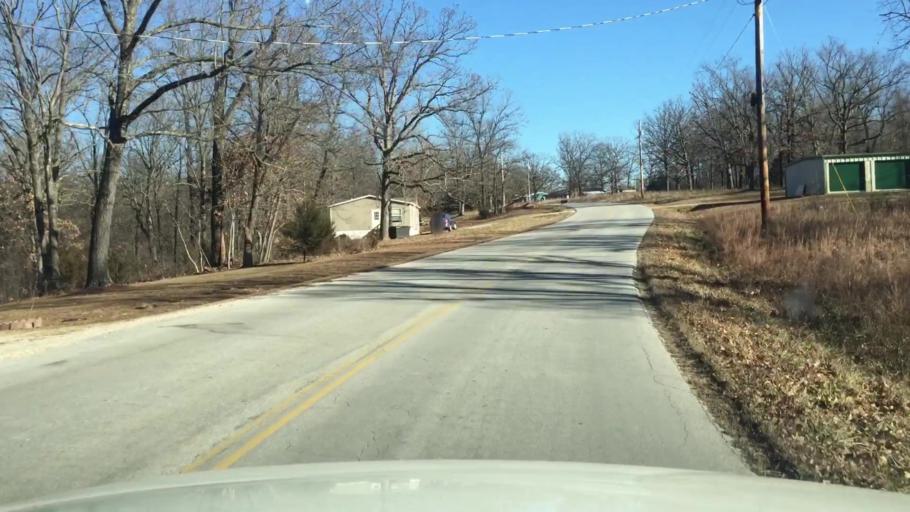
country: US
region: Missouri
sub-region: Morgan County
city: Versailles
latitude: 38.3360
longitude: -92.7662
